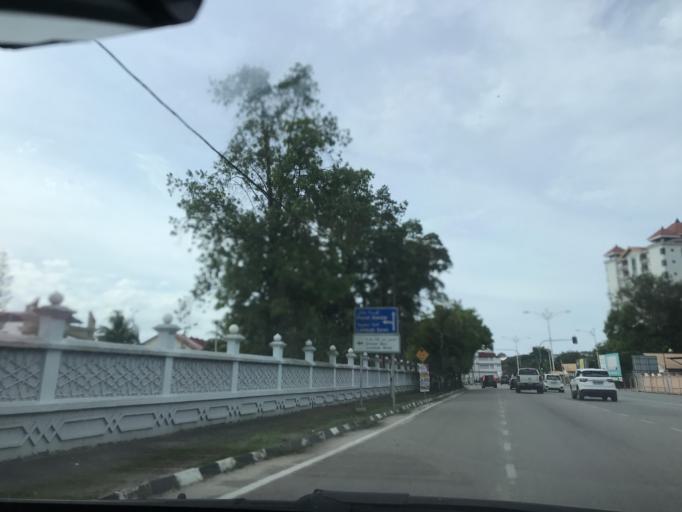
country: MY
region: Kelantan
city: Kota Bharu
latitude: 6.1099
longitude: 102.2373
